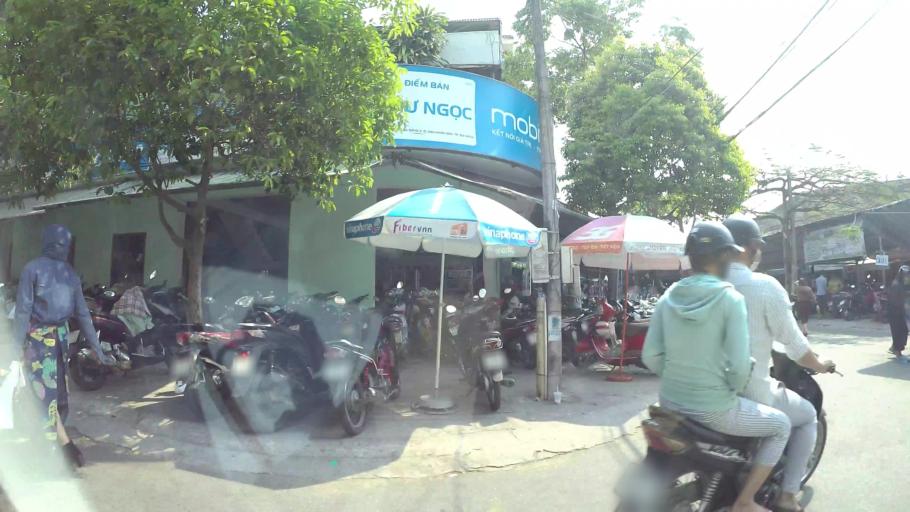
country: VN
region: Da Nang
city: Son Tra
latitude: 16.0419
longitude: 108.2422
